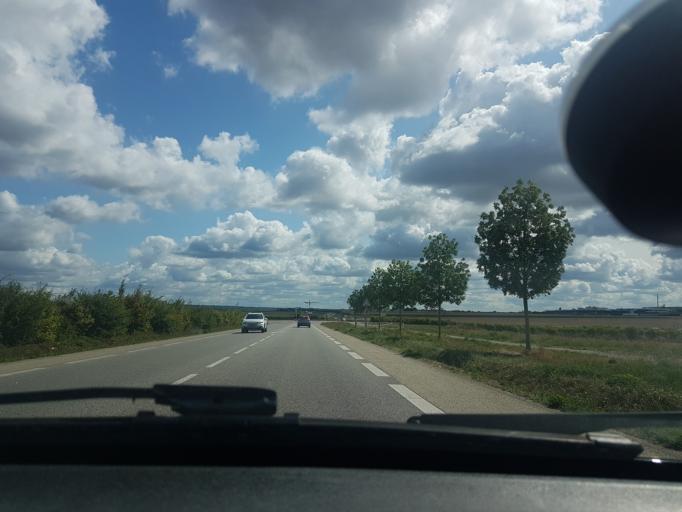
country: FR
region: Ile-de-France
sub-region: Departement des Yvelines
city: Plaisir
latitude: 48.8348
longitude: 1.9677
